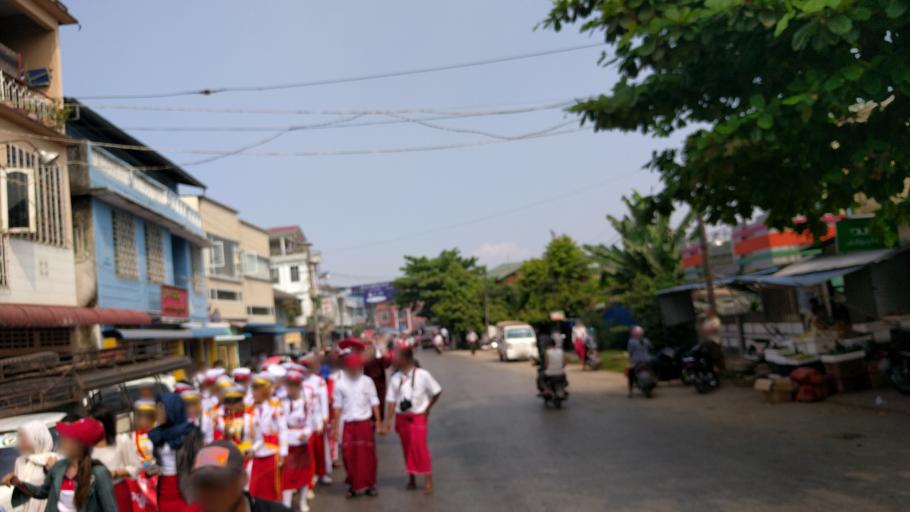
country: MM
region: Mon
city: Mawlamyine
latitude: 16.4744
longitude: 97.6218
